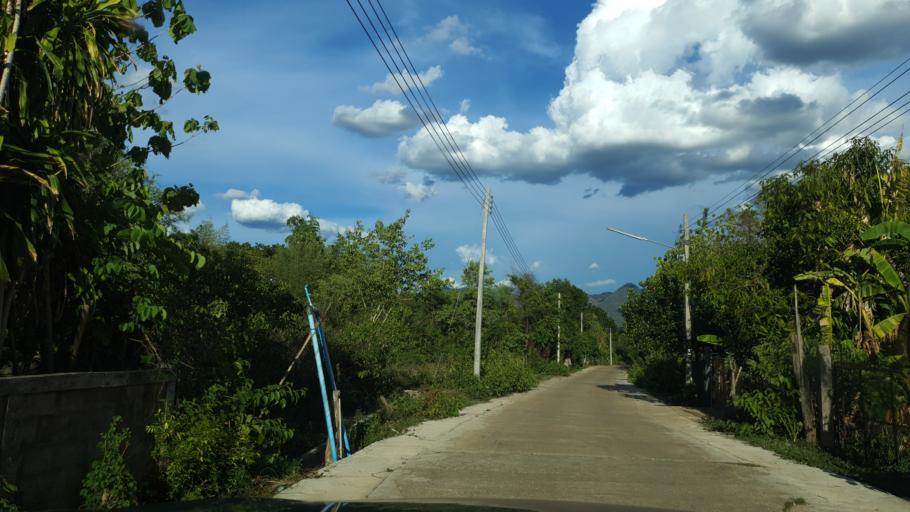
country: TH
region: Lampang
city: Sop Prap
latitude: 17.8751
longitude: 99.3032
